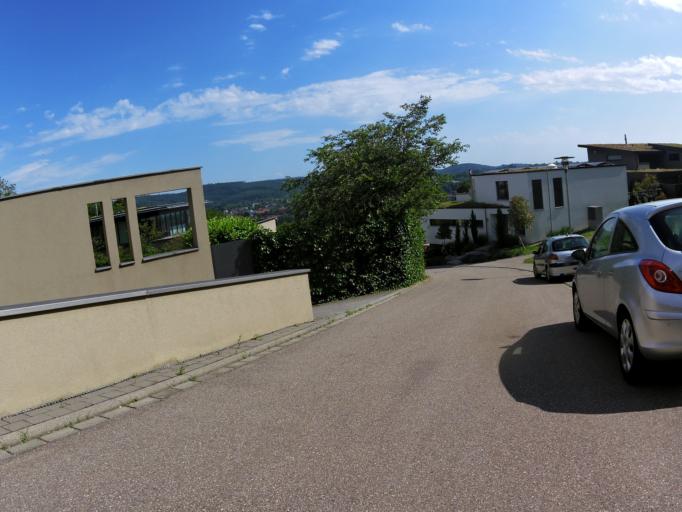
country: DE
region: Baden-Wuerttemberg
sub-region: Freiburg Region
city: Lahr
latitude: 48.3462
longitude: 7.8568
